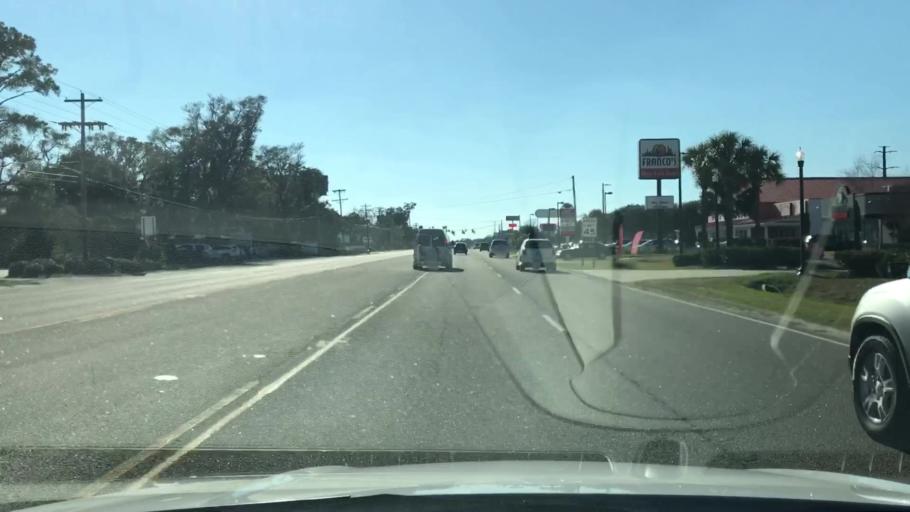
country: US
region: South Carolina
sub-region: Horry County
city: Garden City
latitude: 33.5808
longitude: -79.0195
